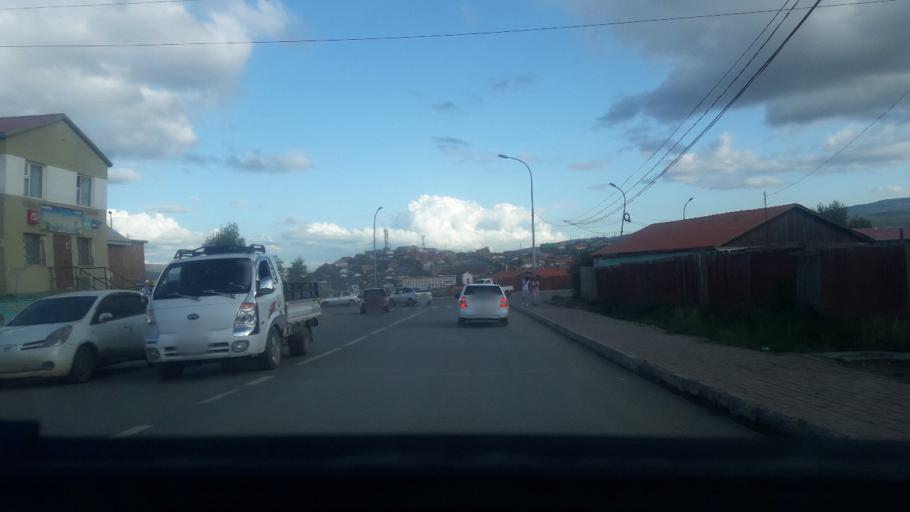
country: MN
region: Ulaanbaatar
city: Ulaanbaatar
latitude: 47.9331
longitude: 107.0075
